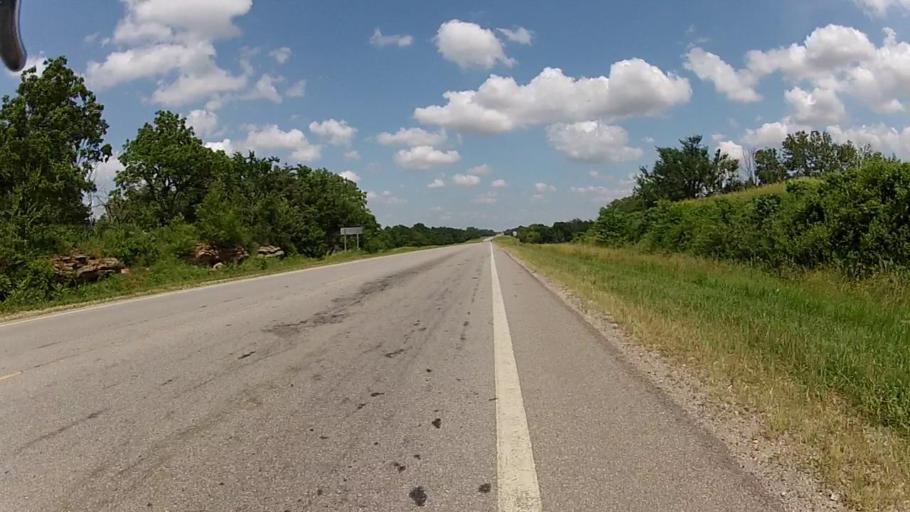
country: US
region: Kansas
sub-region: Labette County
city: Altamont
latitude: 37.1935
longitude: -95.2112
